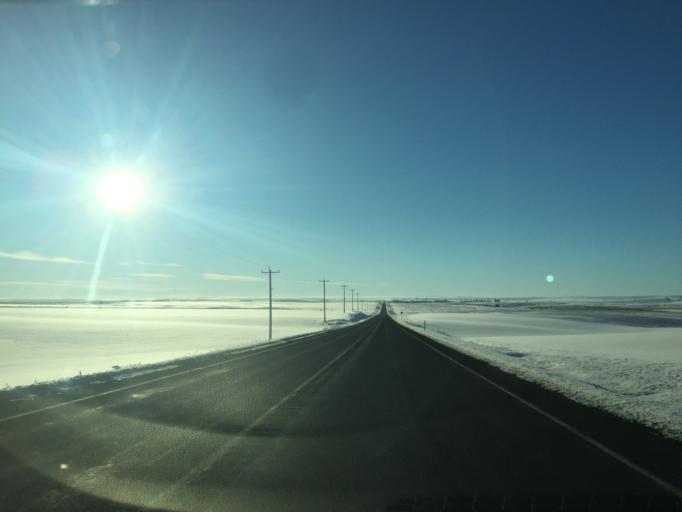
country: US
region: Washington
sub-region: Okanogan County
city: Coulee Dam
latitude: 47.7303
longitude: -118.8691
